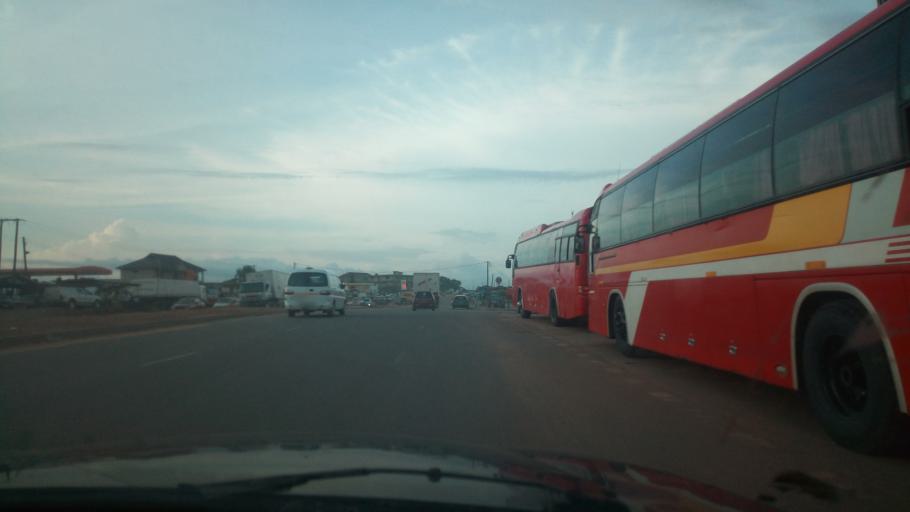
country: GH
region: Western
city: Takoradi
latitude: 4.9116
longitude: -1.7940
